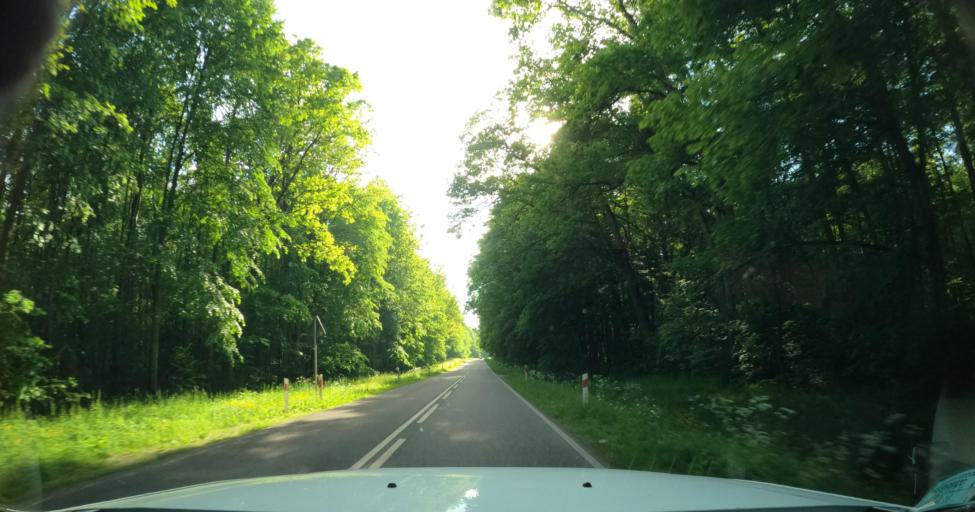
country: PL
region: Warmian-Masurian Voivodeship
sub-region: Powiat elblaski
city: Paslek
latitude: 54.0794
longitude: 19.7311
